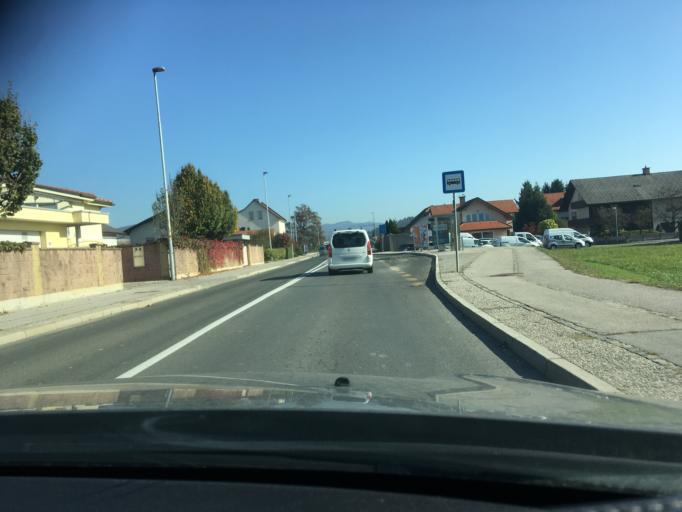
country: SI
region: Domzale
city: Dob
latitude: 46.1549
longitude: 14.6310
